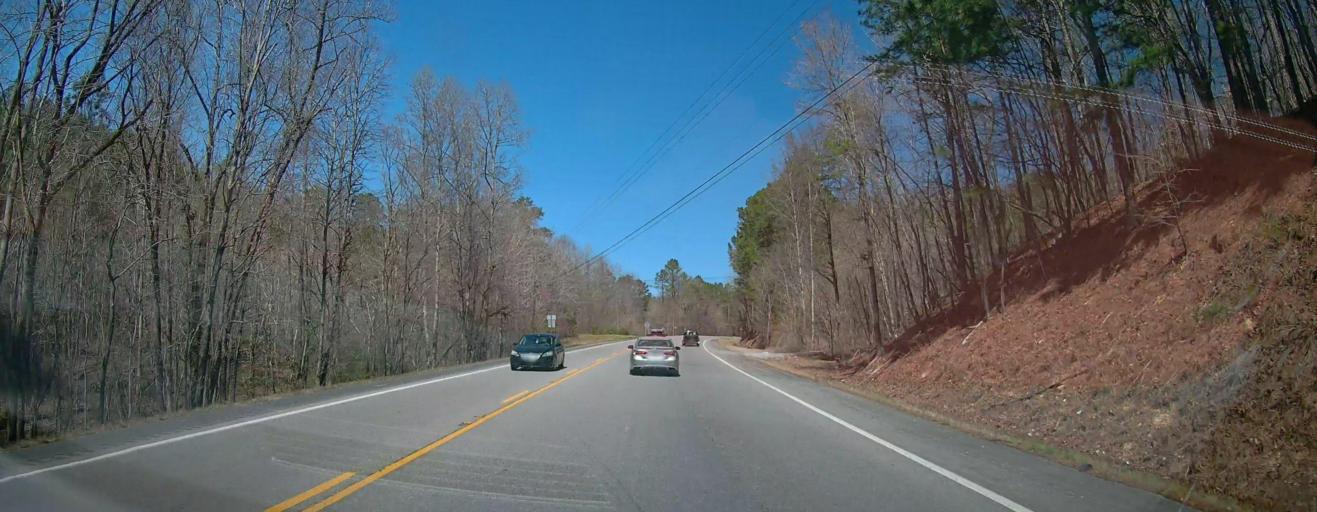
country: US
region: Alabama
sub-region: Calhoun County
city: Ohatchee
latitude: 33.8391
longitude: -86.0506
